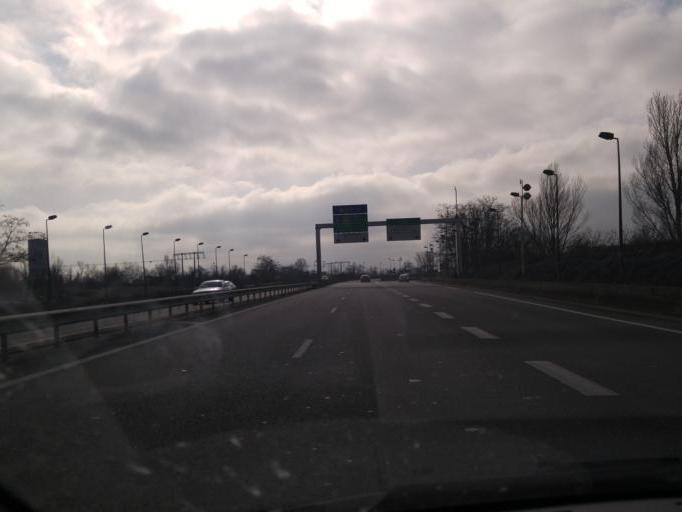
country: FR
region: Midi-Pyrenees
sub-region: Departement de la Haute-Garonne
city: Blagnac
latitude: 43.6125
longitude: 1.3866
